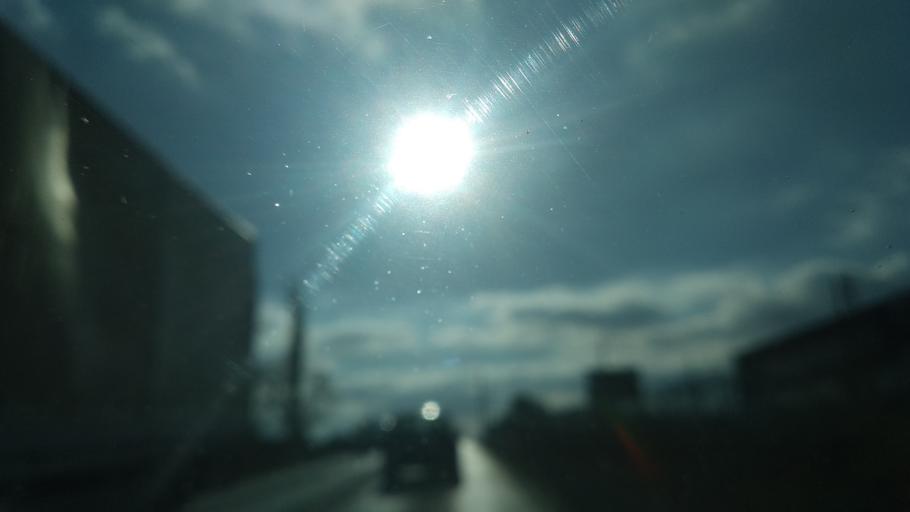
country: XK
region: Pristina
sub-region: Komuna e Prishtines
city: Pristina
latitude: 42.7378
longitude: 21.1418
